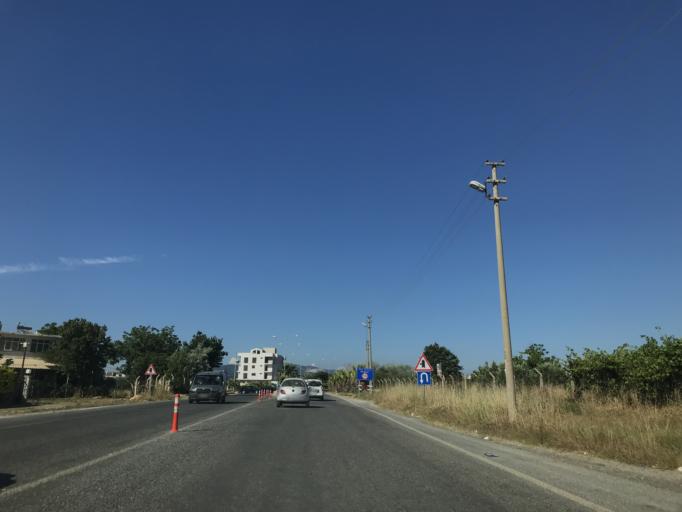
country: TR
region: Aydin
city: Davutlar
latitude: 37.7317
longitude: 27.2727
